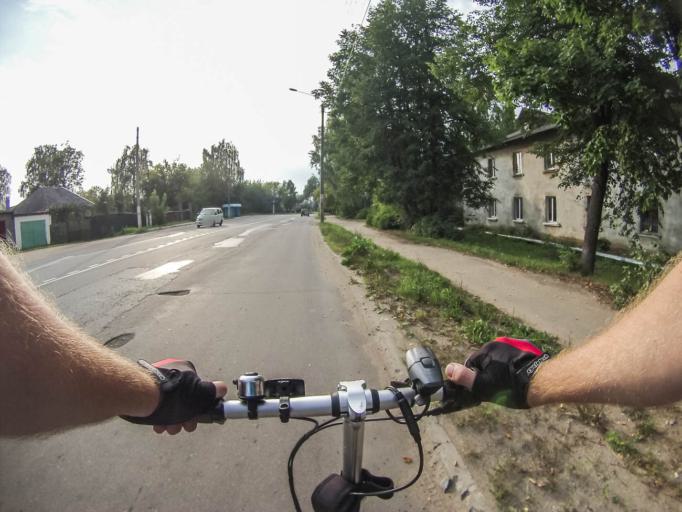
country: RU
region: Kostroma
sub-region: Kostromskoy Rayon
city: Kostroma
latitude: 57.7834
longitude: 40.8750
